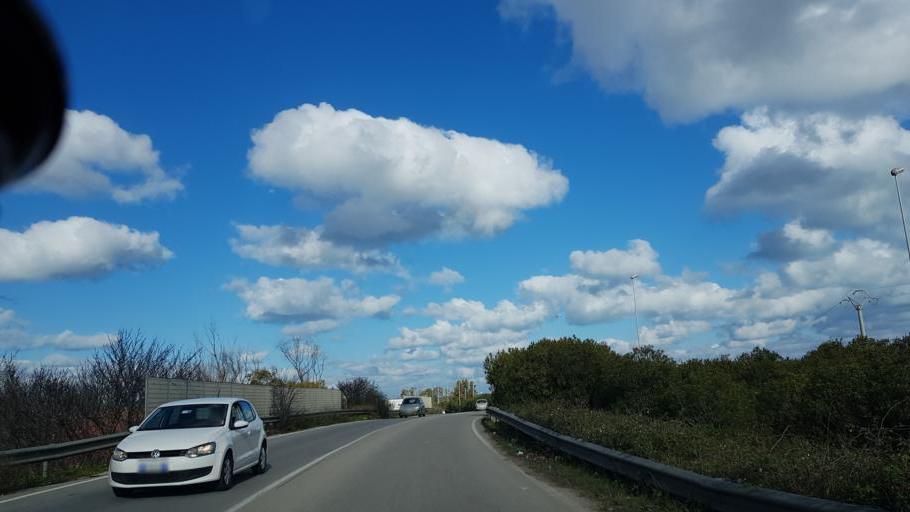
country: IT
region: Apulia
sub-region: Provincia di Brindisi
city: Brindisi
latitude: 40.6307
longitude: 17.9186
